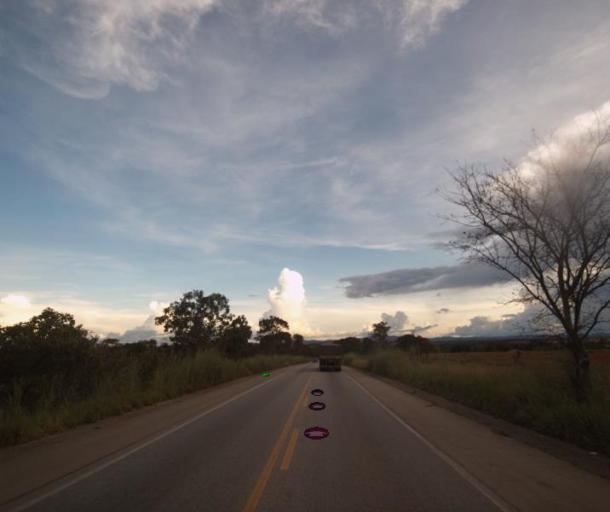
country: BR
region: Goias
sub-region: Uruacu
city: Uruacu
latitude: -14.2346
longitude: -49.1351
